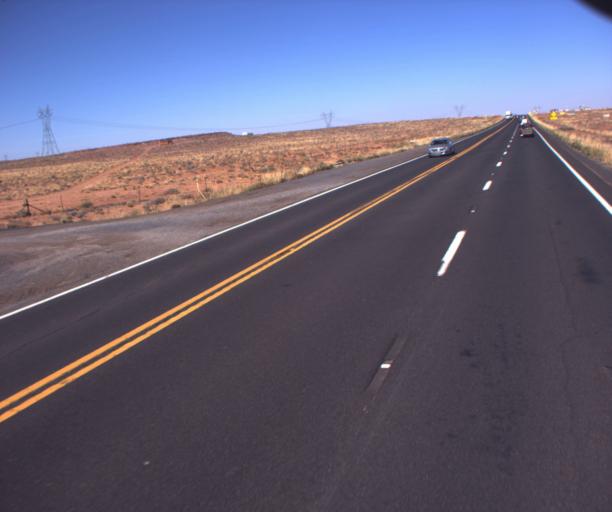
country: US
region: Arizona
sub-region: Coconino County
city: Tuba City
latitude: 35.8039
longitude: -111.4455
